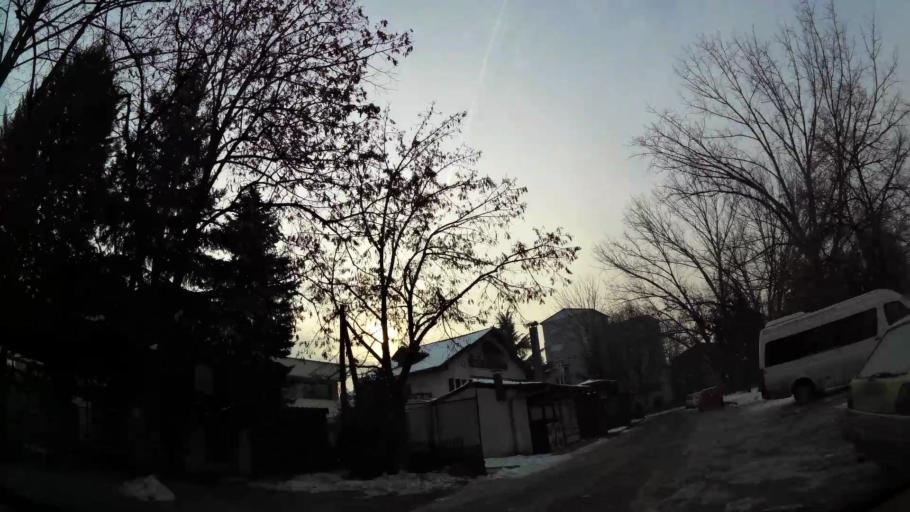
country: MK
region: Cair
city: Cair
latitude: 42.0228
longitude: 21.4446
